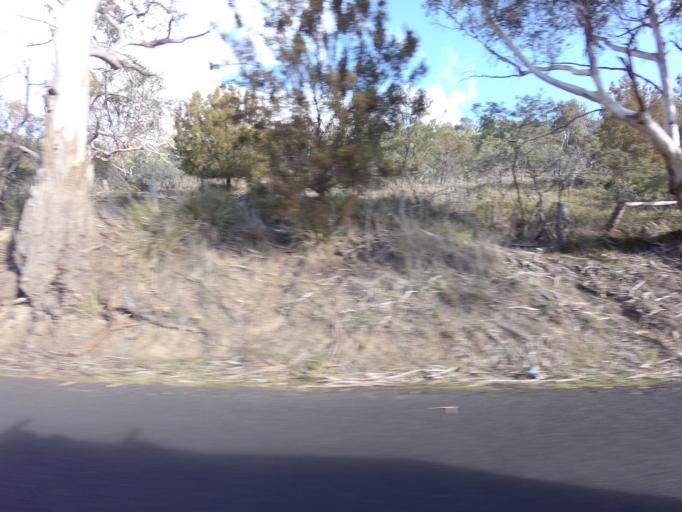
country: AU
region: Tasmania
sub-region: Derwent Valley
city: New Norfolk
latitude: -42.7448
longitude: 147.0395
